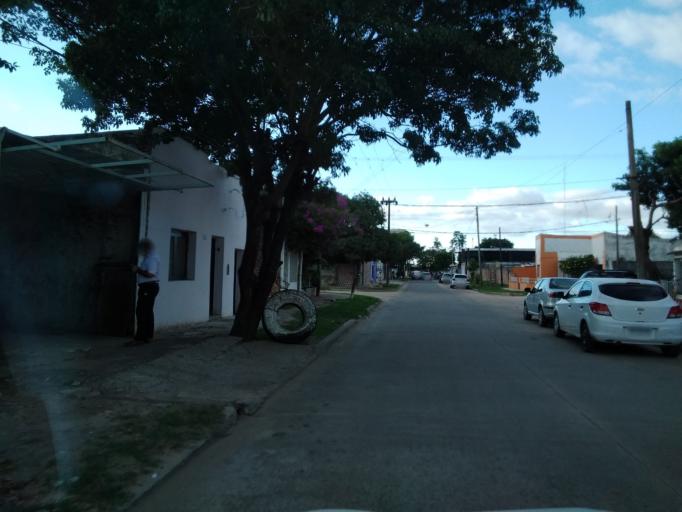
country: AR
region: Corrientes
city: Corrientes
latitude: -27.4743
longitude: -58.8055
